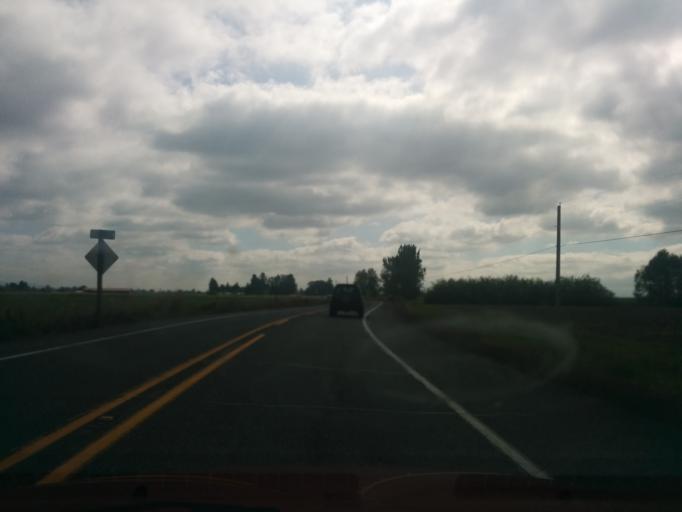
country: US
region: Washington
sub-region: Whatcom County
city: Sudden Valley
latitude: 48.5950
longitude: -122.4218
